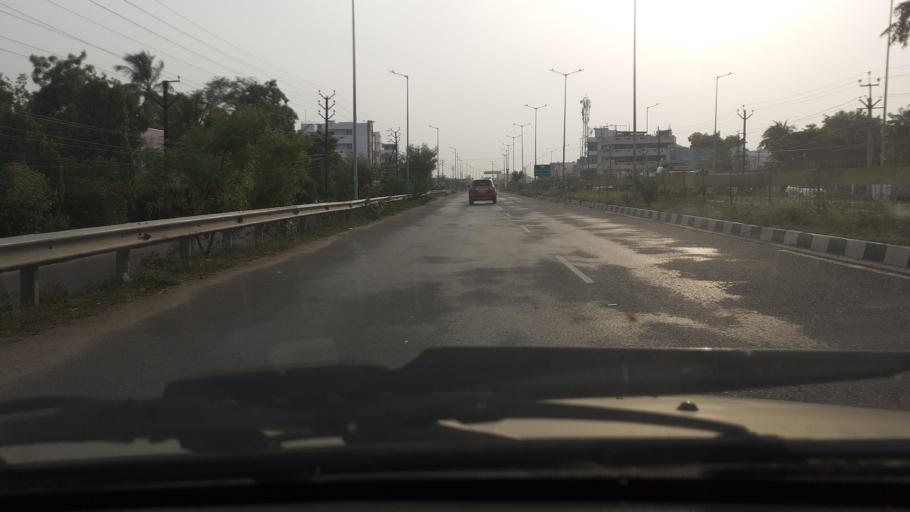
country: IN
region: Tamil Nadu
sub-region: Tirunelveli Kattabo
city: Tirunelveli
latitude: 8.7137
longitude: 77.7756
